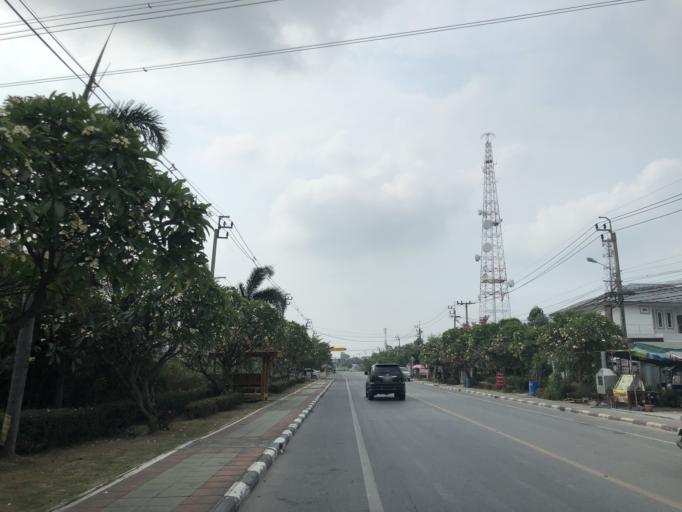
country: TH
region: Samut Prakan
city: Bang Bo District
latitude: 13.5851
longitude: 100.7425
